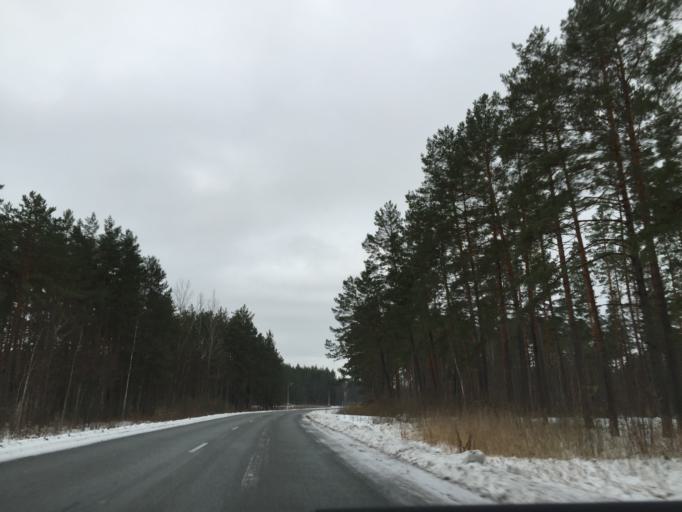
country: LV
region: Saulkrastu
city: Saulkrasti
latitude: 57.2097
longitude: 24.3812
